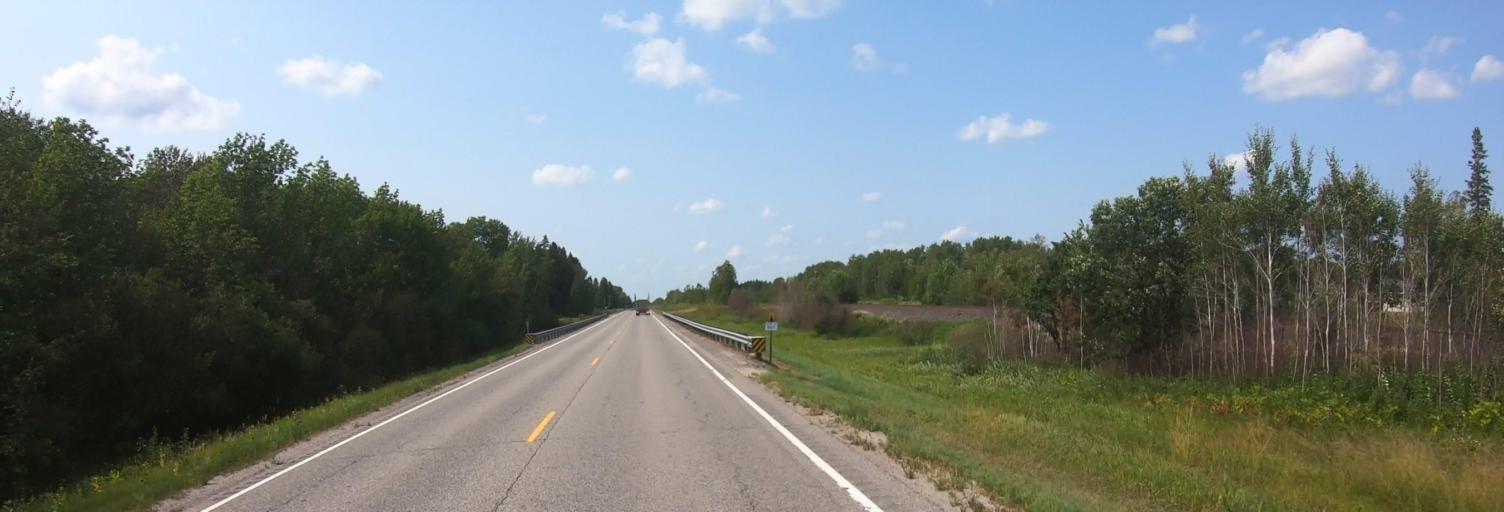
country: US
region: Minnesota
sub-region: Roseau County
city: Warroad
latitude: 48.8089
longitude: -95.1134
